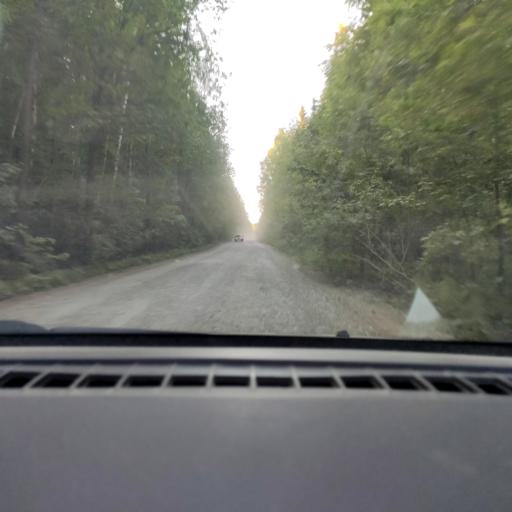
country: RU
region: Perm
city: Polazna
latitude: 58.1259
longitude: 56.4367
